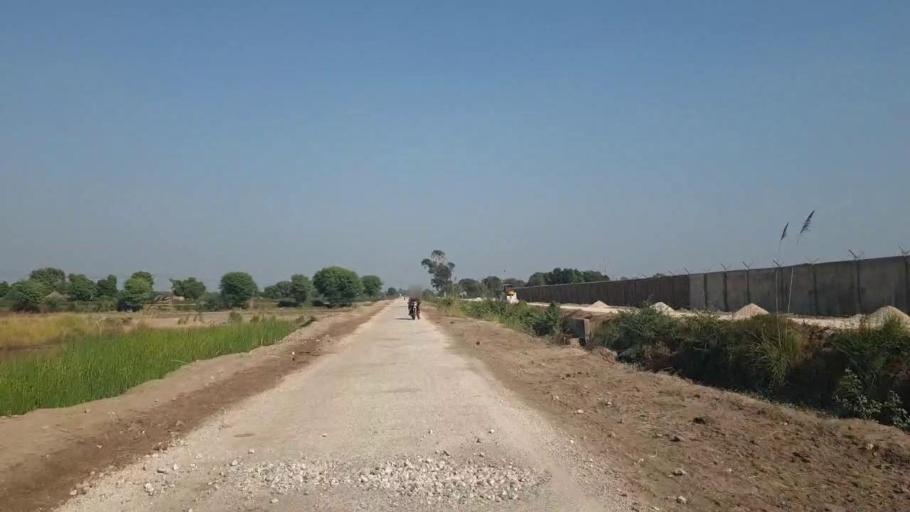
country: PK
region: Sindh
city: Hyderabad
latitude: 25.4745
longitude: 68.3907
